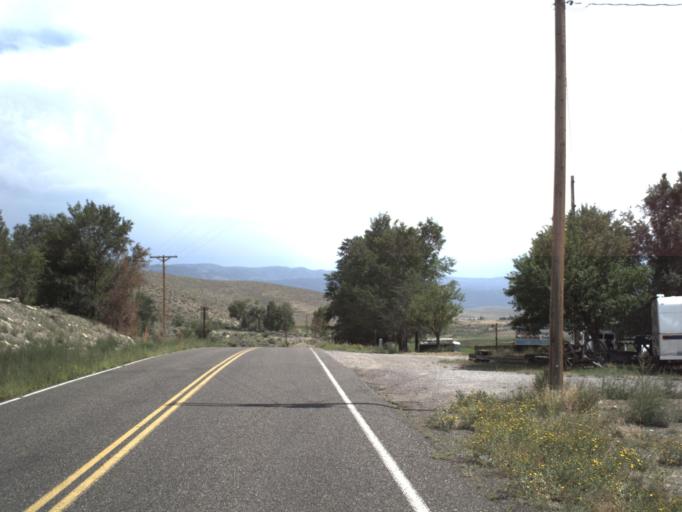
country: US
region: Utah
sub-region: Piute County
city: Junction
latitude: 38.1142
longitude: -111.9922
